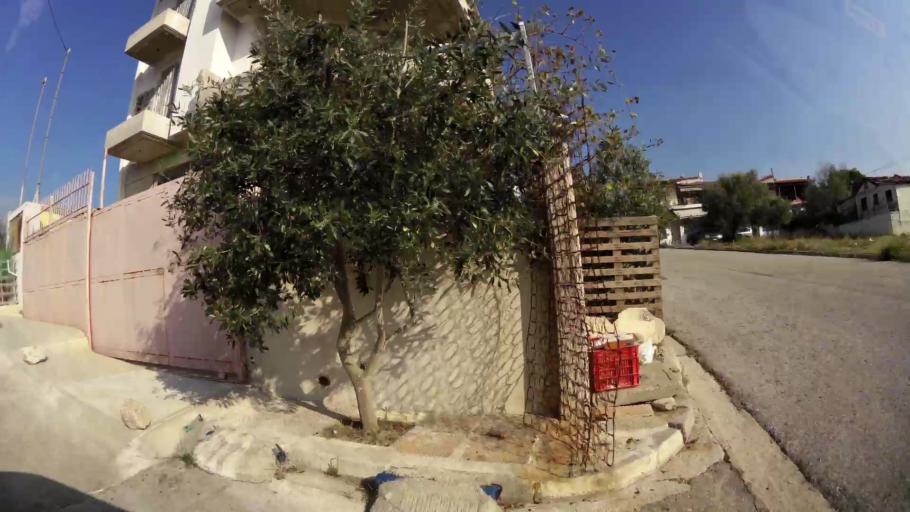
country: GR
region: Attica
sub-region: Nomarchia Dytikis Attikis
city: Zefyri
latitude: 38.0693
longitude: 23.7266
